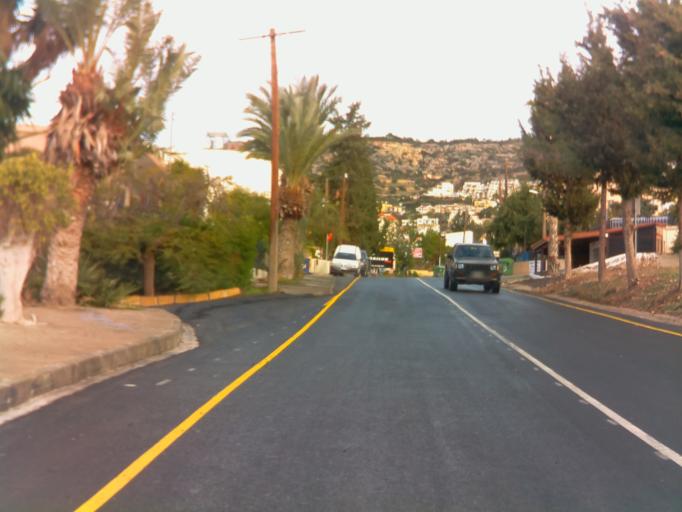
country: CY
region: Pafos
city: Pegeia
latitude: 34.8778
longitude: 32.3801
